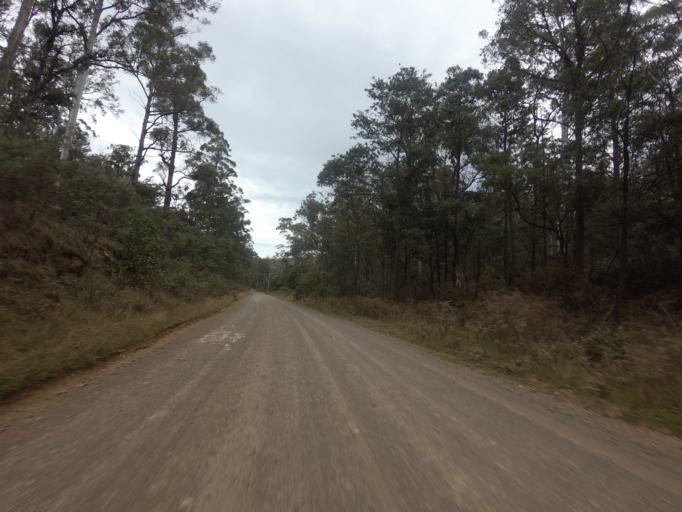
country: AU
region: Tasmania
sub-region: Derwent Valley
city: New Norfolk
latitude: -42.5835
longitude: 147.0090
